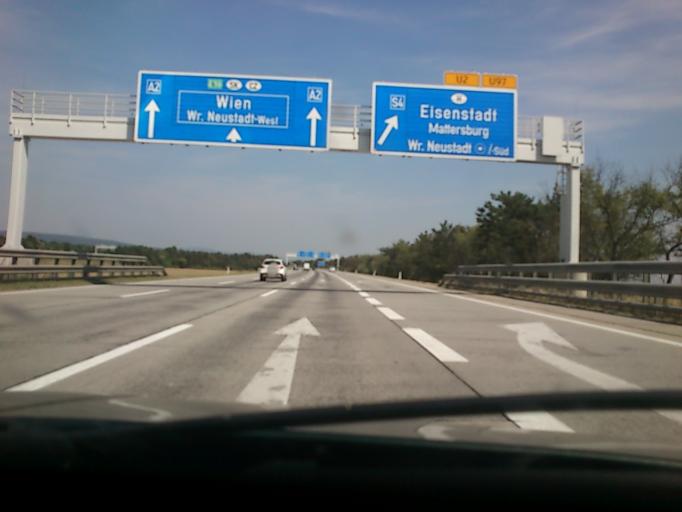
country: AT
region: Lower Austria
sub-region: Wiener Neustadt Stadt
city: Wiener Neustadt
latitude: 47.7790
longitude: 16.2063
